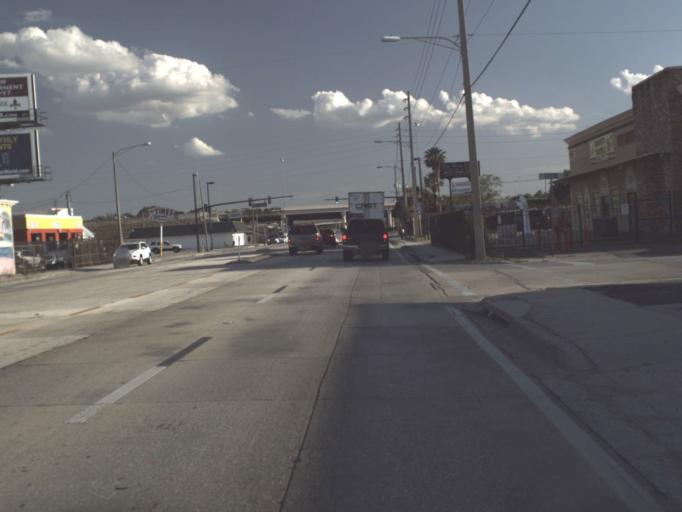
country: US
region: Florida
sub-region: Orange County
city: Holden Heights
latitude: 28.5139
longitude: -81.3971
